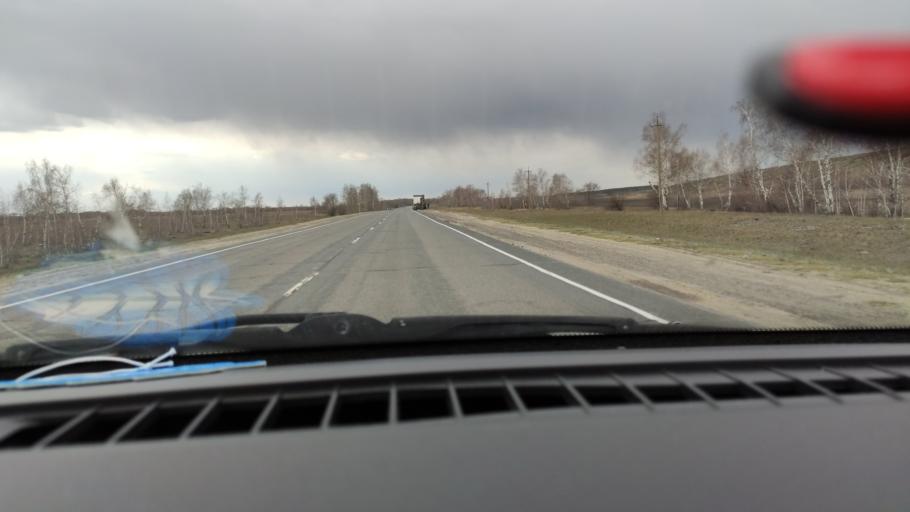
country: RU
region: Saratov
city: Sinodskoye
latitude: 52.0550
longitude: 46.7573
